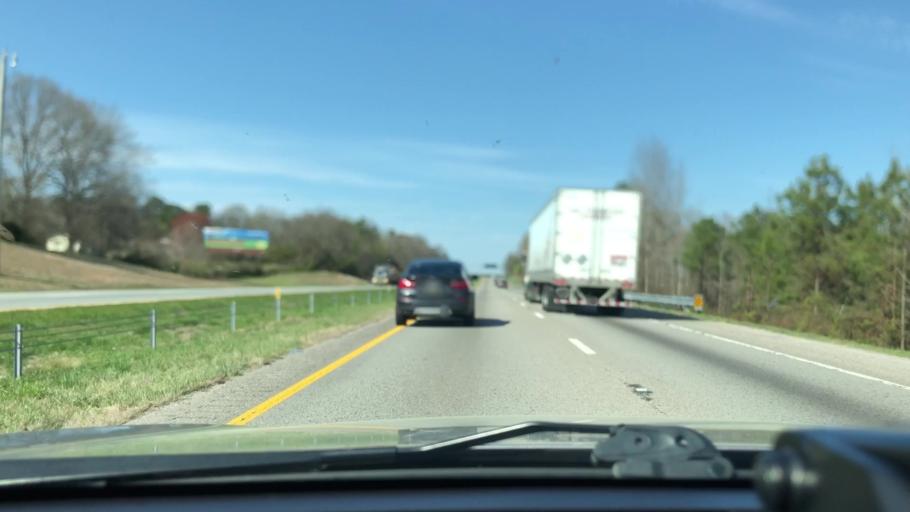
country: US
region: South Carolina
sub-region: Spartanburg County
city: Roebuck
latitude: 34.8912
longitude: -81.9931
